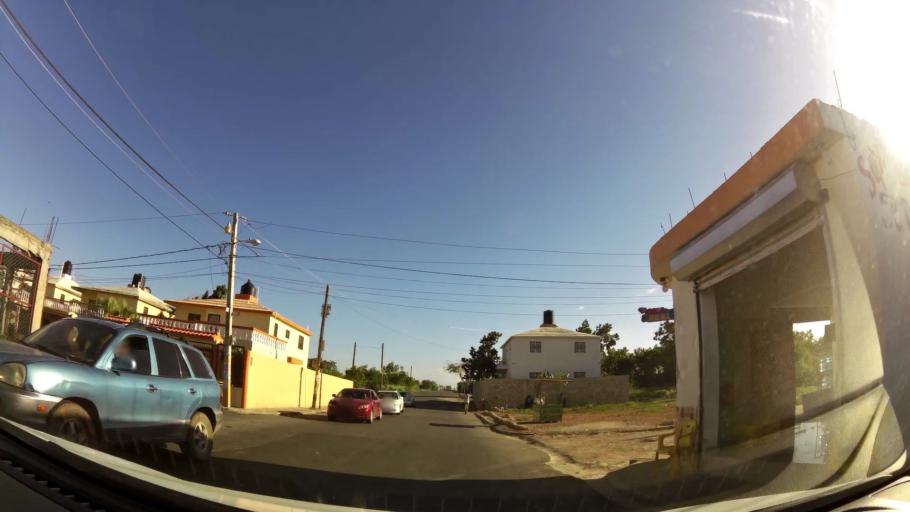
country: DO
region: Santo Domingo
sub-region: Santo Domingo
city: Santo Domingo Este
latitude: 18.4842
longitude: -69.8057
